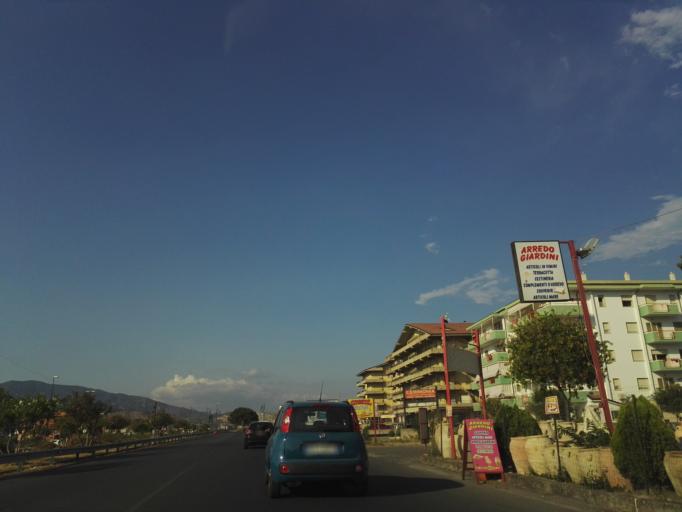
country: IT
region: Calabria
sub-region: Provincia di Reggio Calabria
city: Marina di Gioiosa Ionica
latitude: 38.2925
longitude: 16.3201
